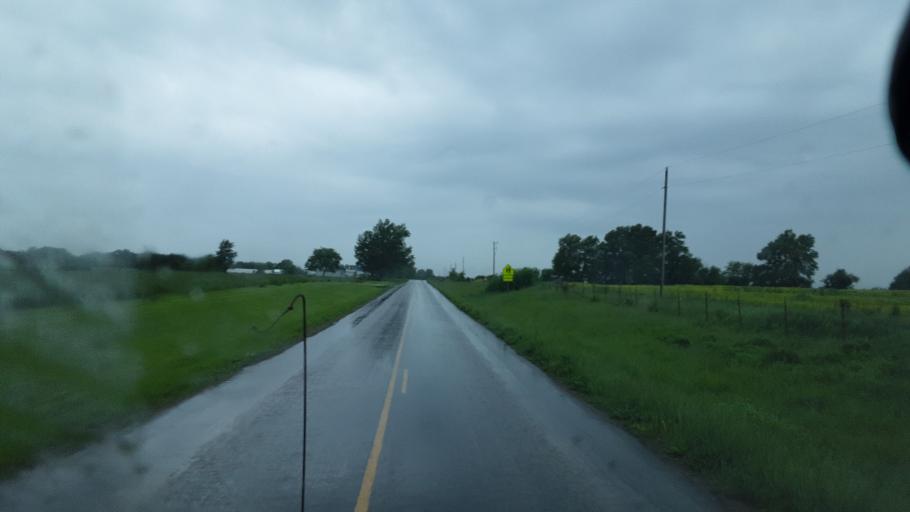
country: US
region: Missouri
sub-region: Randolph County
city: Moberly
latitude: 39.3680
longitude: -92.2560
